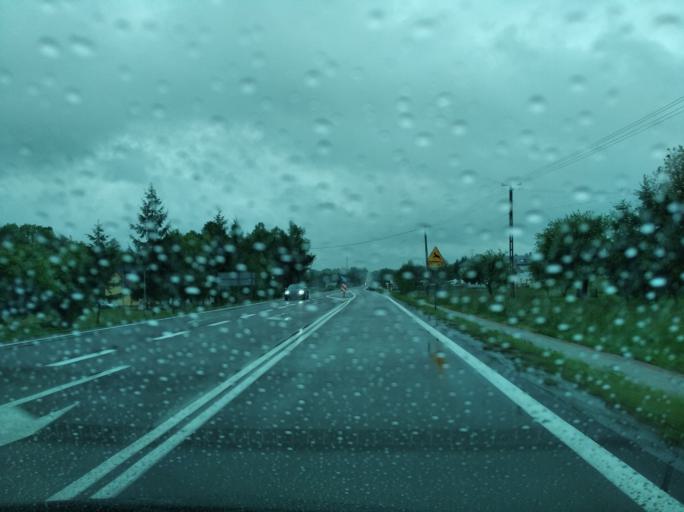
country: PL
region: Subcarpathian Voivodeship
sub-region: Powiat brzozowski
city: Jablonica Polska
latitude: 49.6998
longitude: 21.8800
